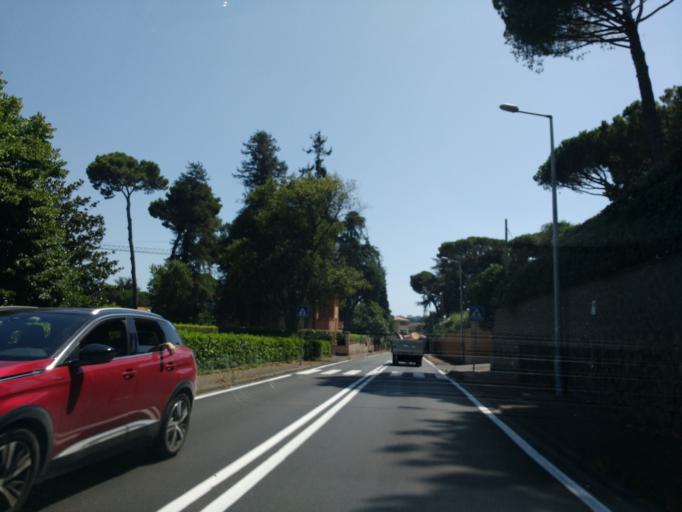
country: IT
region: Latium
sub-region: Citta metropolitana di Roma Capitale
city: Grottaferrata
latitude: 41.7867
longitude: 12.6816
